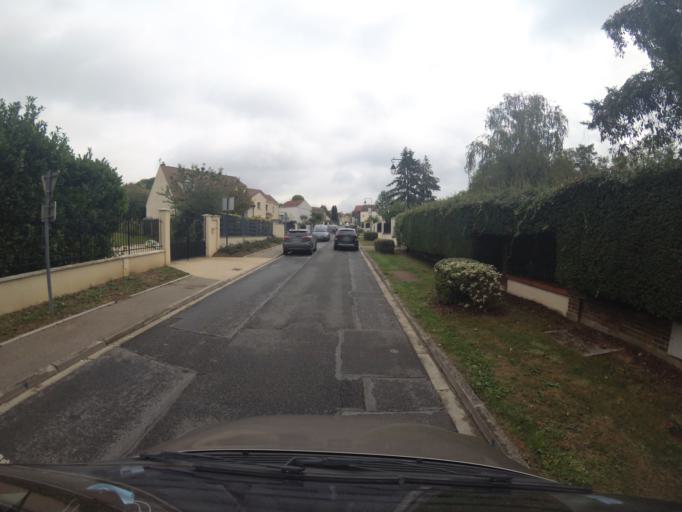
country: FR
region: Ile-de-France
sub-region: Departement de Seine-et-Marne
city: Bussy-Saint-Georges
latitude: 48.8467
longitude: 2.6928
